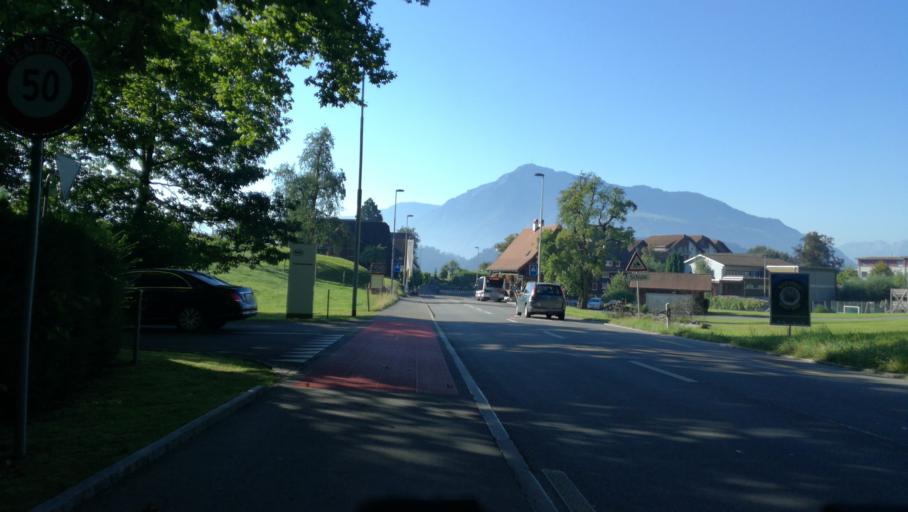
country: CH
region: Lucerne
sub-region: Lucerne-Land District
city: Meierskappel
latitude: 47.1357
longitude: 8.4655
